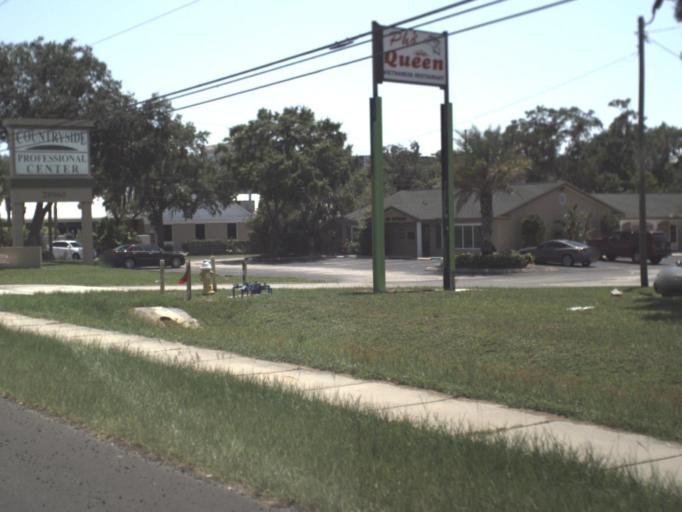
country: US
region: Florida
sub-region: Pinellas County
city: Saint George
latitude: 28.0359
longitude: -82.7384
